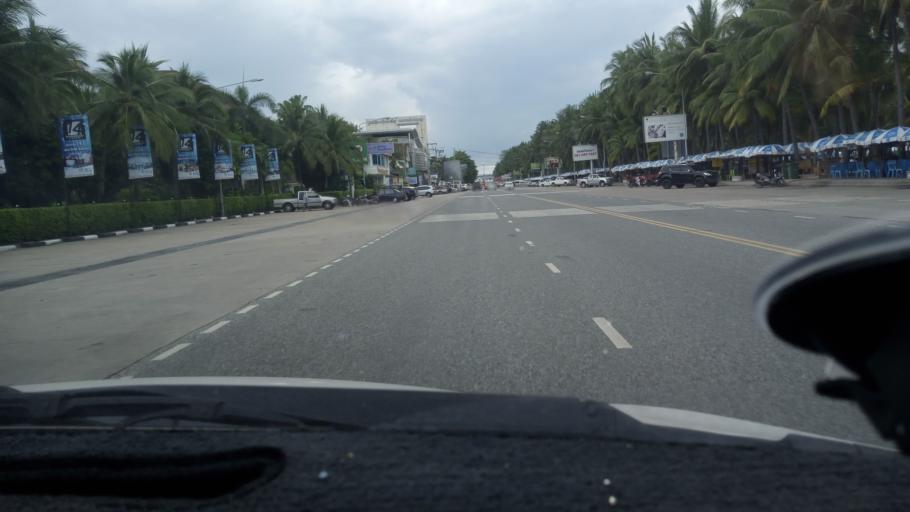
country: TH
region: Chon Buri
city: Chon Buri
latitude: 13.2893
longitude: 100.9112
